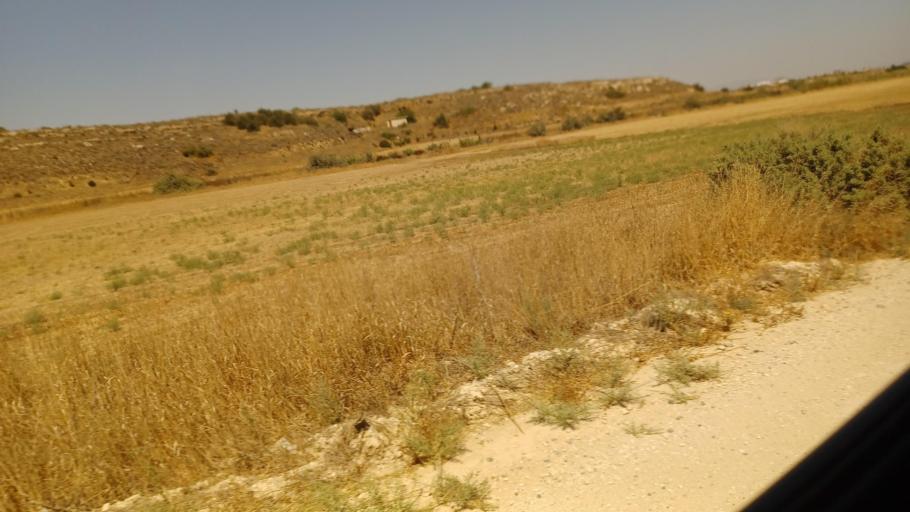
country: CY
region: Ammochostos
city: Acheritou
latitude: 35.0984
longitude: 33.8751
